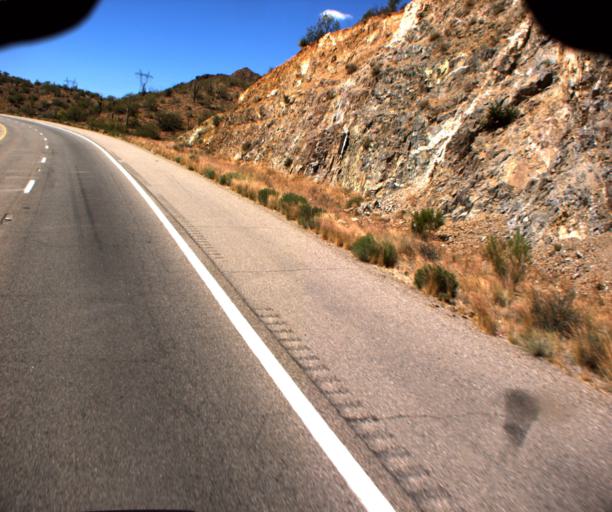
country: US
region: Arizona
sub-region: Yavapai County
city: Bagdad
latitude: 34.4554
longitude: -113.2893
